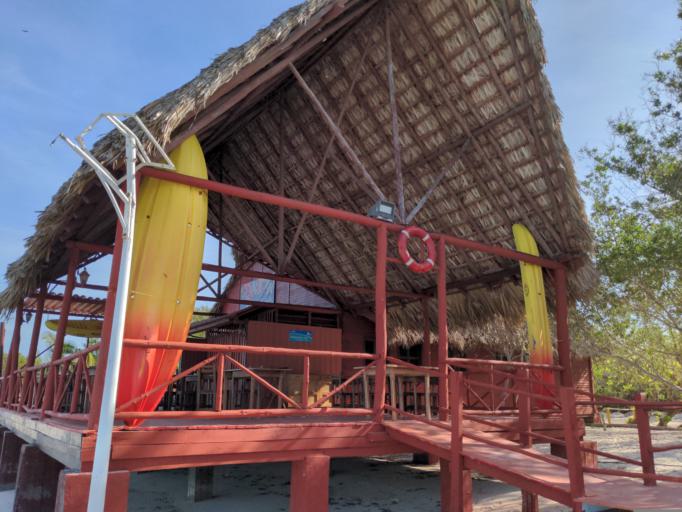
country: CU
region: Pinar del Rio
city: Minas de Matahambre
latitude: 22.7020
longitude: -84.0504
